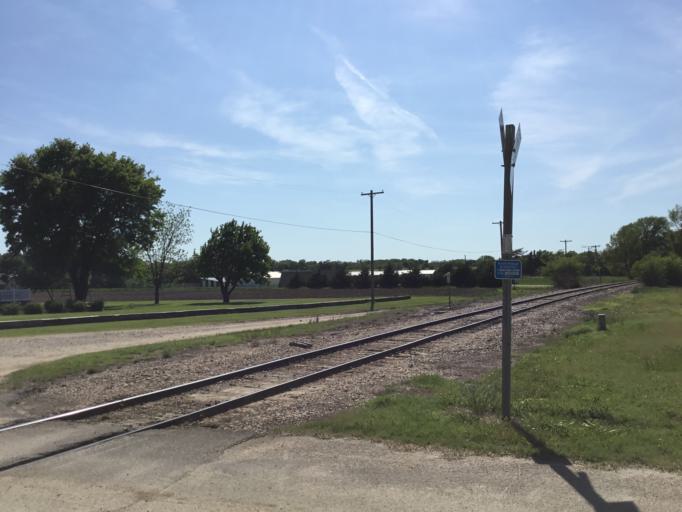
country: US
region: Kansas
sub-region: Mitchell County
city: Beloit
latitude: 39.4570
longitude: -98.1163
